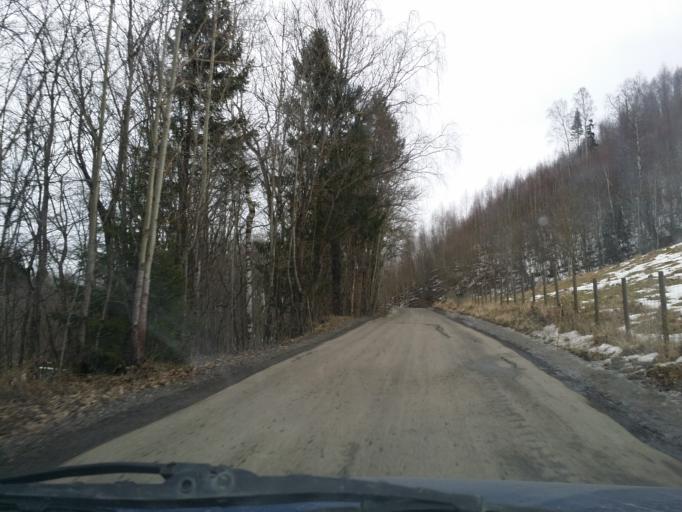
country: NO
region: Buskerud
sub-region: Lier
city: Lierbyen
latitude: 59.8164
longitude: 10.2278
